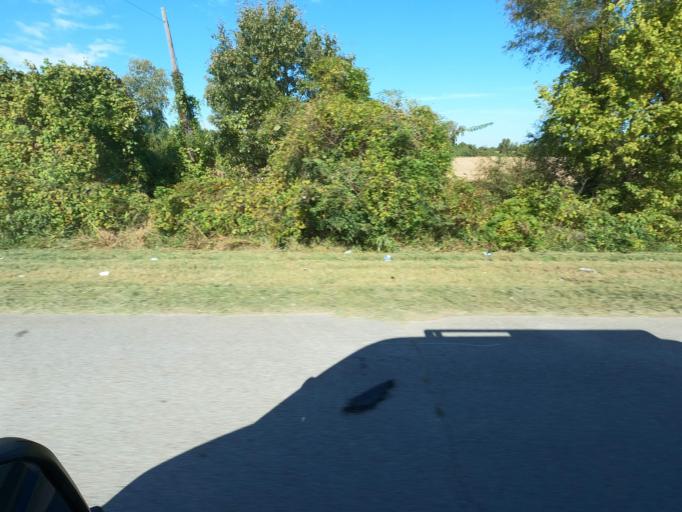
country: US
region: Tennessee
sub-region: Shelby County
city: Millington
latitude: 35.3720
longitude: -89.8805
